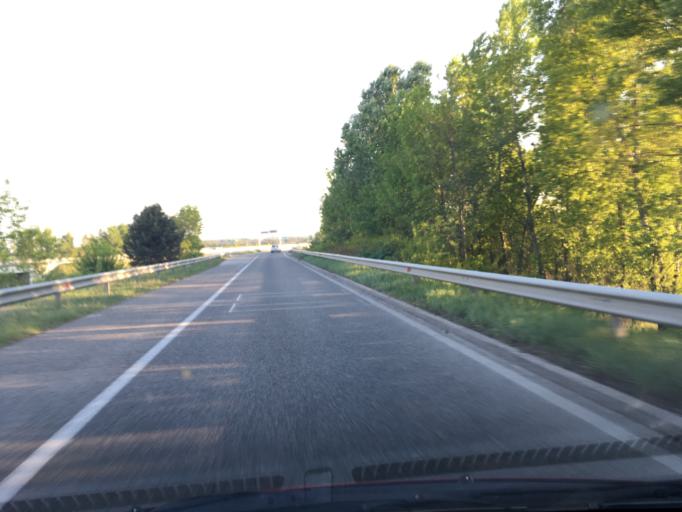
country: HU
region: Budapest
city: Budapest XV. keruelet
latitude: 47.5738
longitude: 19.1554
